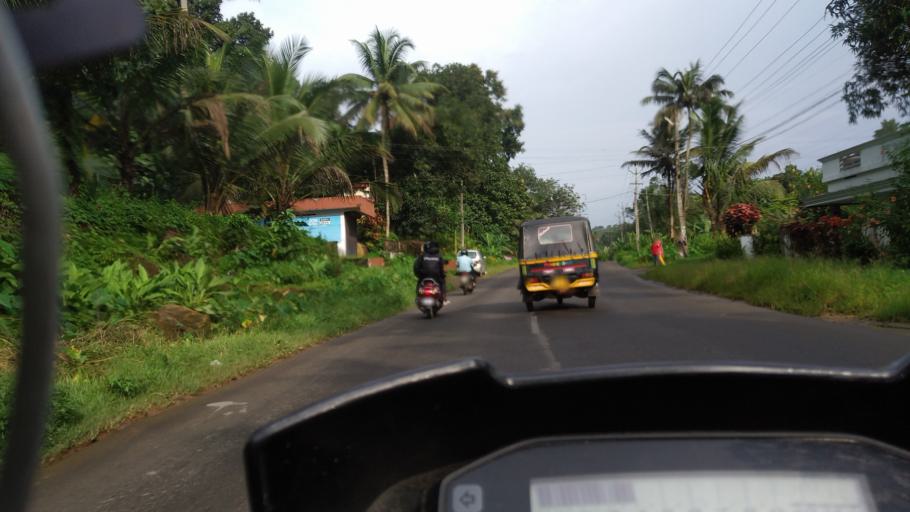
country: IN
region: Kerala
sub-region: Ernakulam
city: Kotamangalam
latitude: 10.0532
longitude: 76.7019
